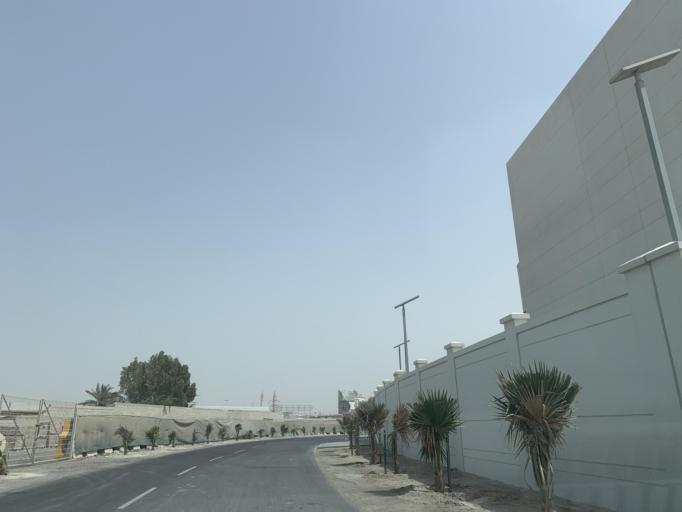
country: BH
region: Northern
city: Madinat `Isa
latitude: 26.1883
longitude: 50.5319
